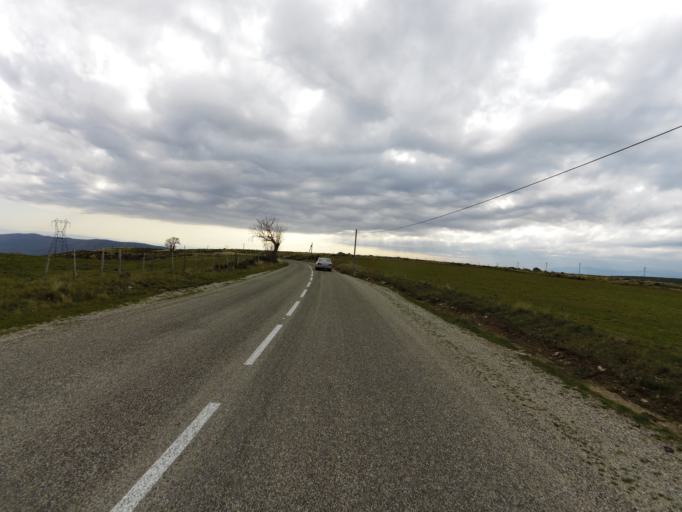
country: FR
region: Rhone-Alpes
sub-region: Departement de l'Ardeche
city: Les Vans
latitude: 44.5538
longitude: 4.0198
